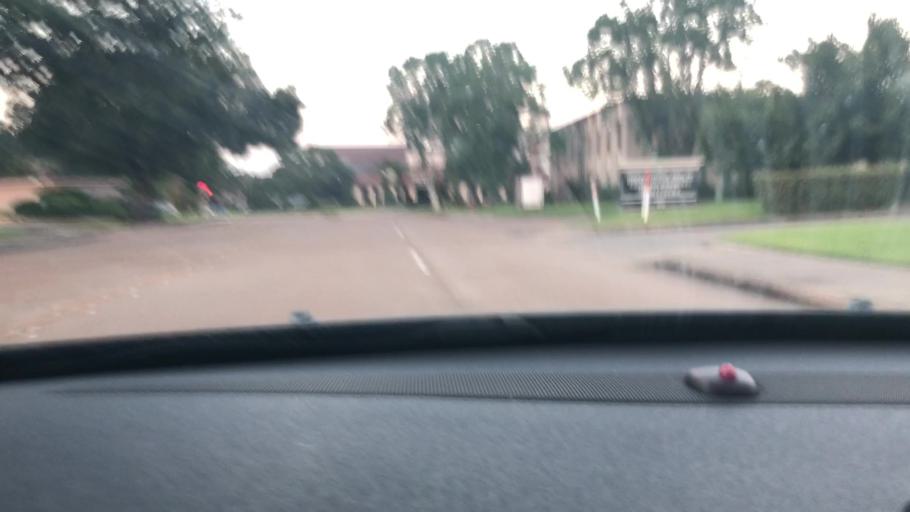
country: US
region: Texas
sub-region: Harris County
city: Webster
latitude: 29.5515
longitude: -95.1175
